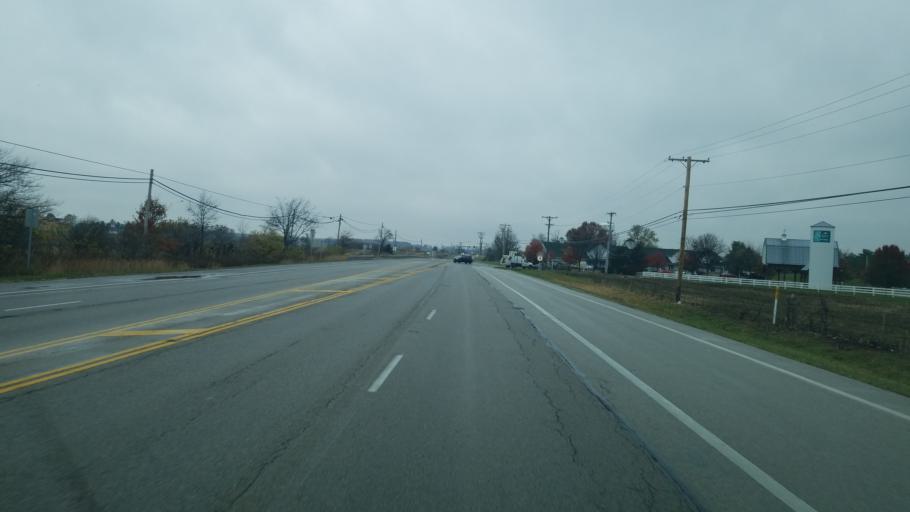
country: US
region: Ohio
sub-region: Union County
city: Marysville
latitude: 40.2577
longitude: -83.3663
